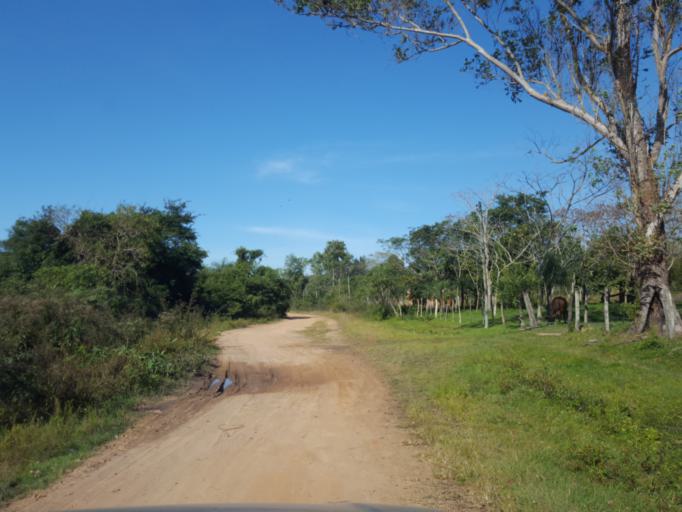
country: PY
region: Cordillera
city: Atyra
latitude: -25.2480
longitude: -57.1236
